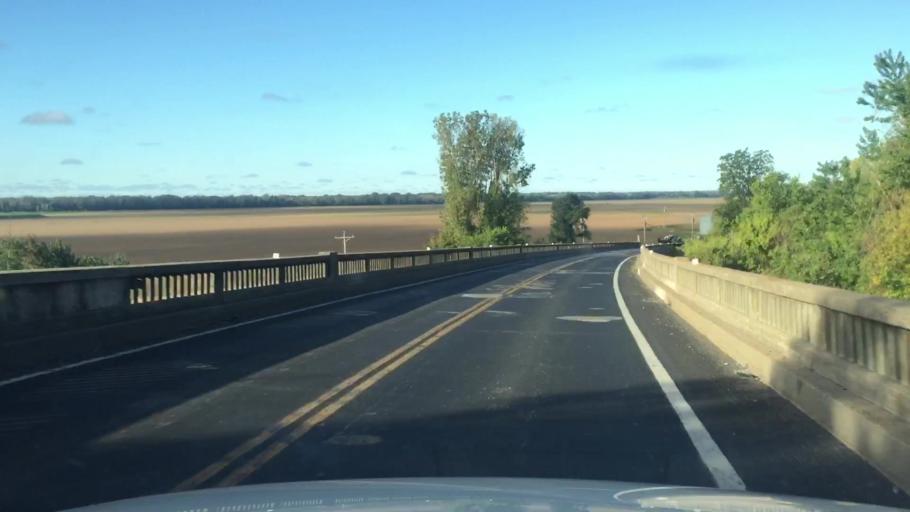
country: US
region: Missouri
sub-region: Howard County
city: New Franklin
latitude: 38.9924
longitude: -92.6160
